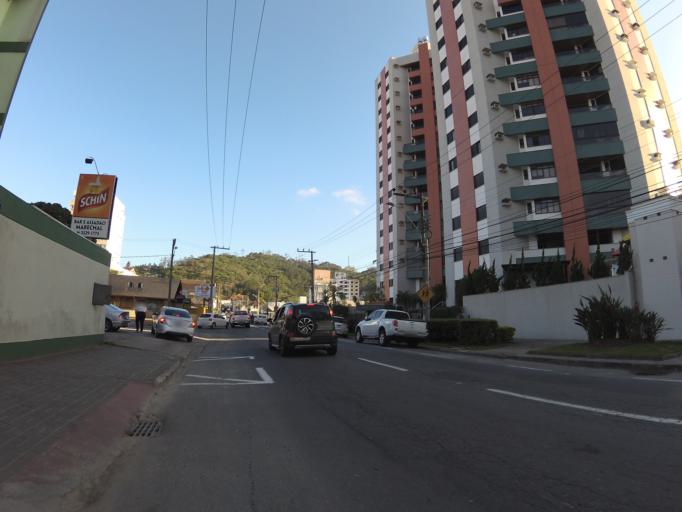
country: BR
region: Santa Catarina
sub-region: Blumenau
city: Blumenau
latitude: -26.9164
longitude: -49.0910
